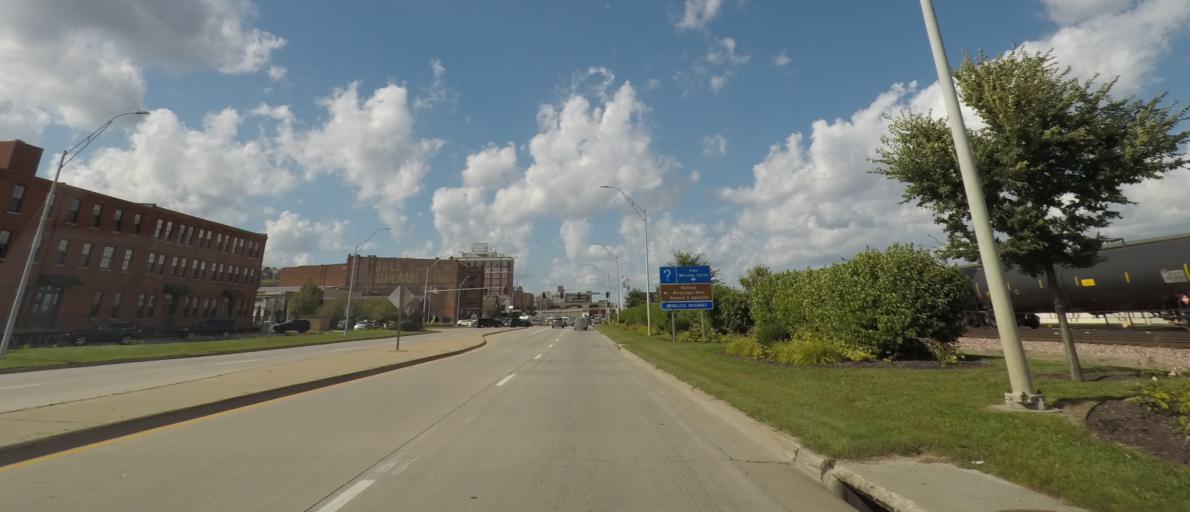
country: US
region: Iowa
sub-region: Dubuque County
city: Dubuque
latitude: 42.4933
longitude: -90.6626
